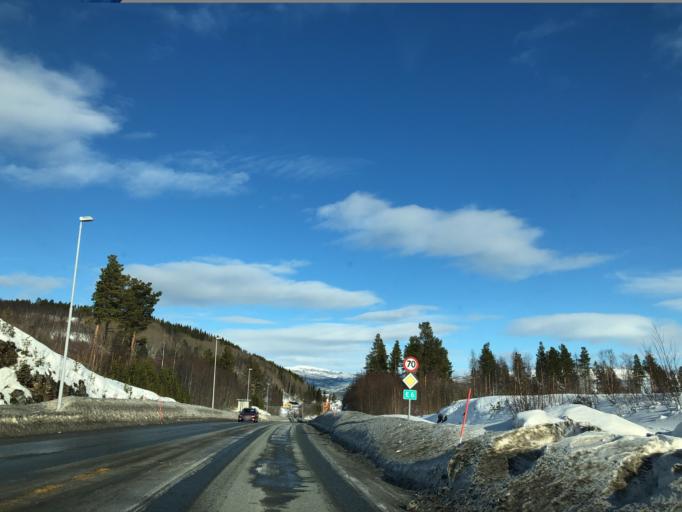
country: NO
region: Troms
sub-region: Malselv
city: Moen
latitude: 69.0616
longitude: 18.4952
